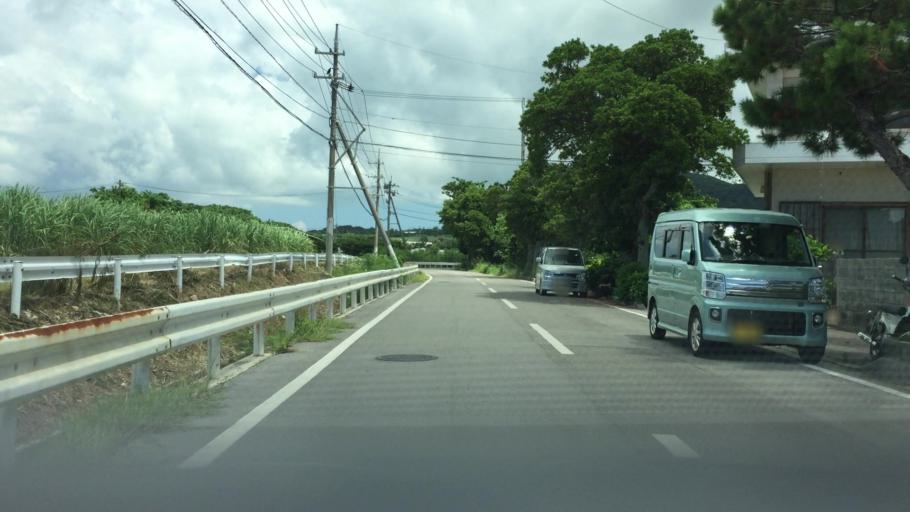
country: JP
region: Okinawa
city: Ishigaki
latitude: 24.3572
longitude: 124.1386
